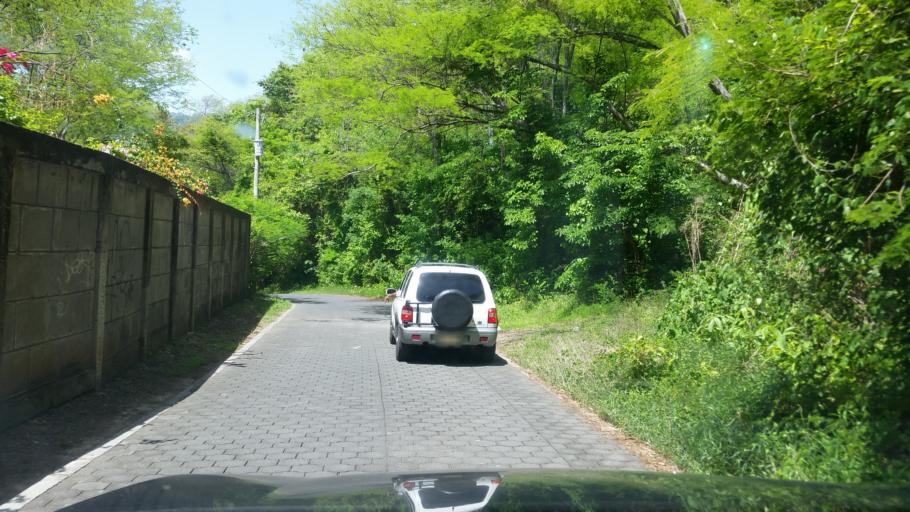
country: NI
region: Masaya
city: Catarina
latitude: 11.9213
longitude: -86.0573
